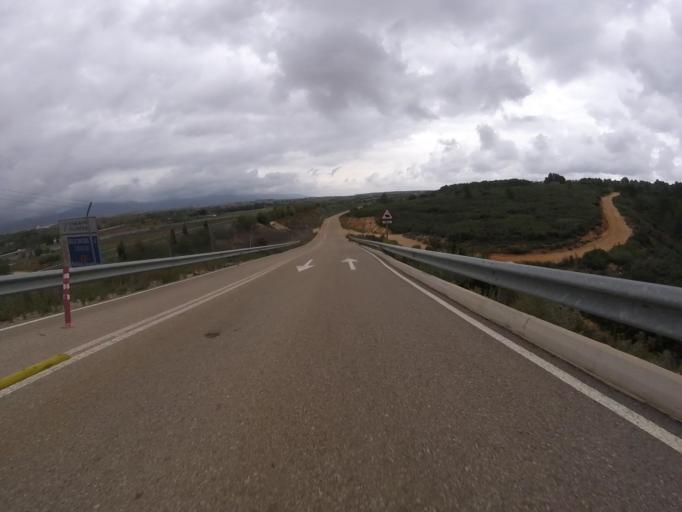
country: ES
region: Valencia
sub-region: Provincia de Castello
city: Benlloch
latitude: 40.1896
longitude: 0.0481
